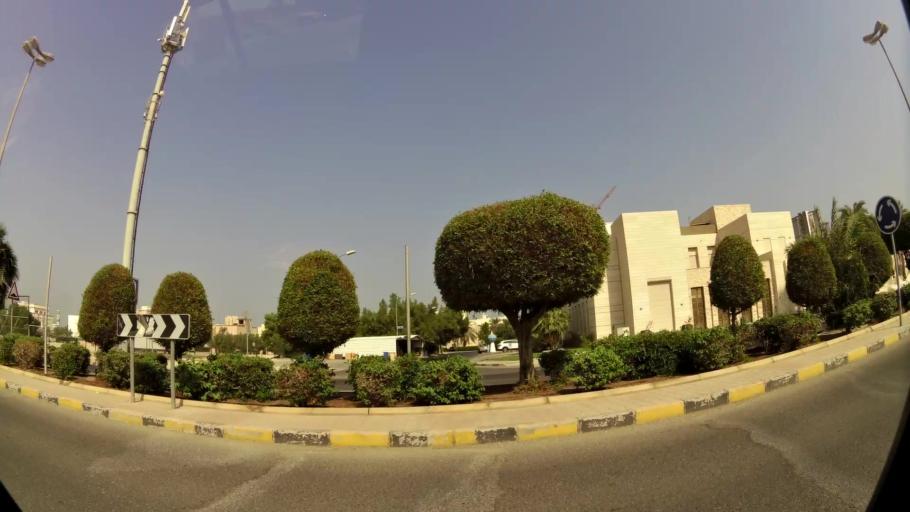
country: KW
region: Muhafazat Hawalli
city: Hawalli
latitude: 29.3538
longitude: 48.0213
